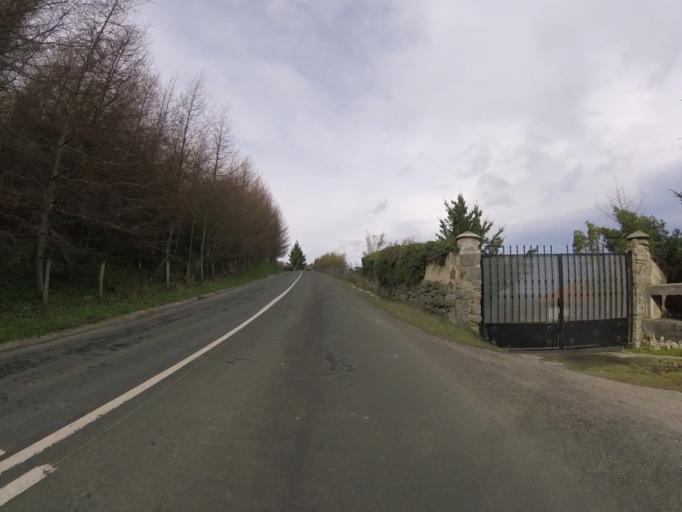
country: ES
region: Basque Country
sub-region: Provincia de Guipuzcoa
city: Errezil
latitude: 43.1505
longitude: -2.1875
